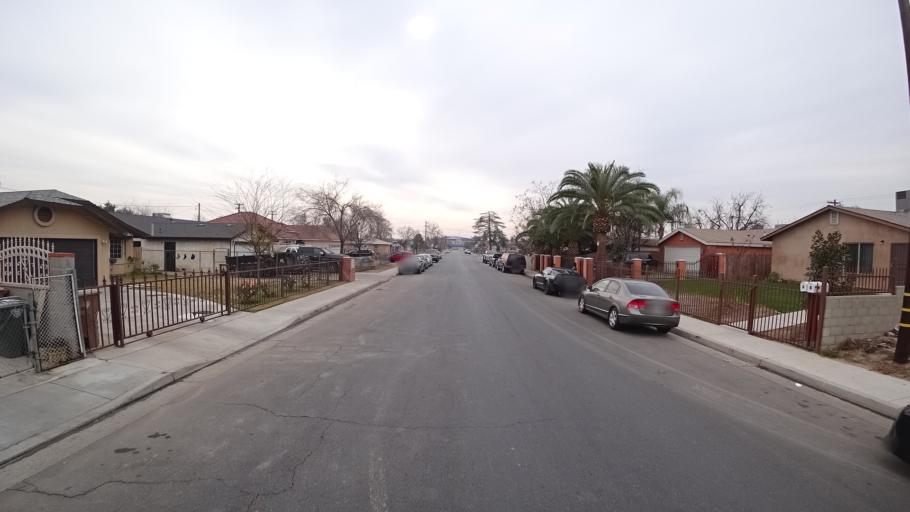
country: US
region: California
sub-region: Kern County
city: Bakersfield
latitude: 35.3567
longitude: -118.9886
